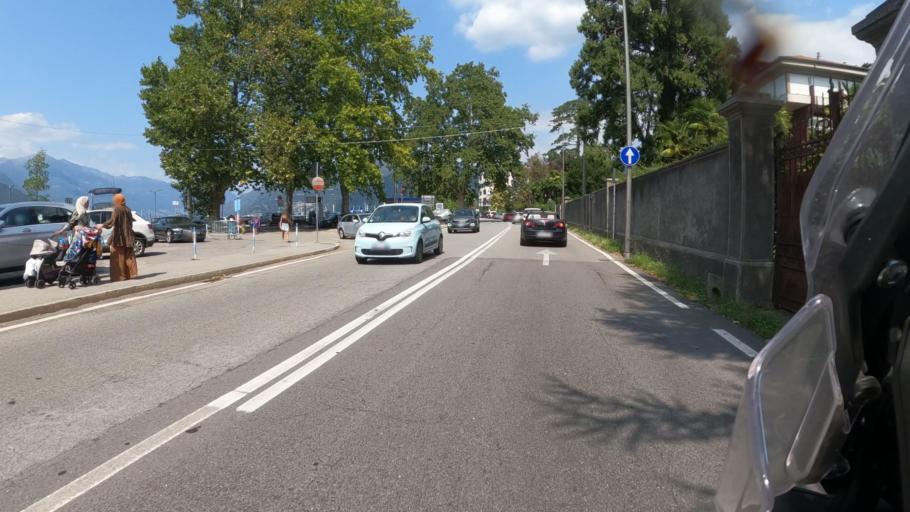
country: IT
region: Lombardy
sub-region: Provincia di Varese
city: Germignaga
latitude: 45.9969
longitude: 8.7338
